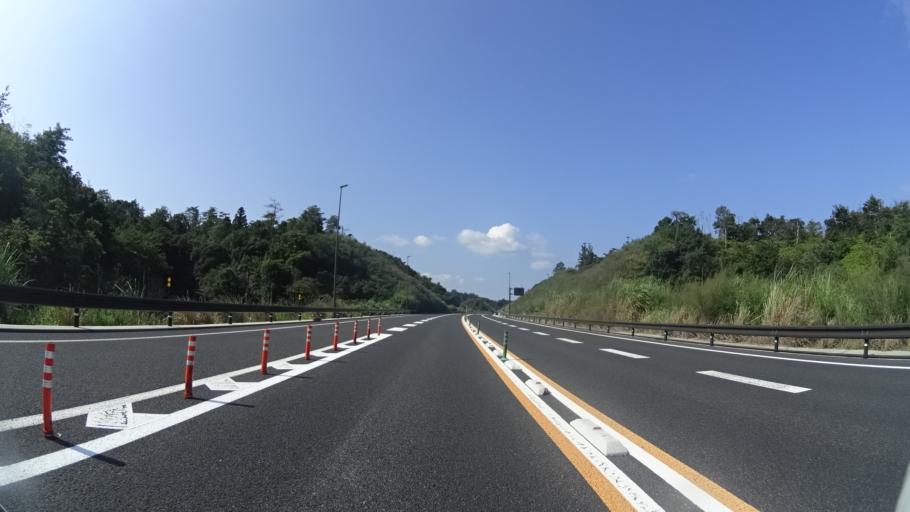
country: JP
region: Shimane
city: Gotsucho
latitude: 35.0811
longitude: 132.3426
